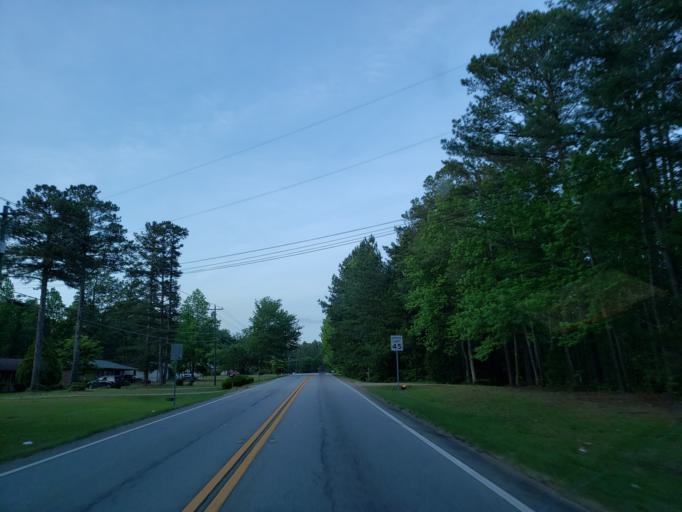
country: US
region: Georgia
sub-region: Douglas County
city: Douglasville
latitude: 33.6641
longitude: -84.8087
